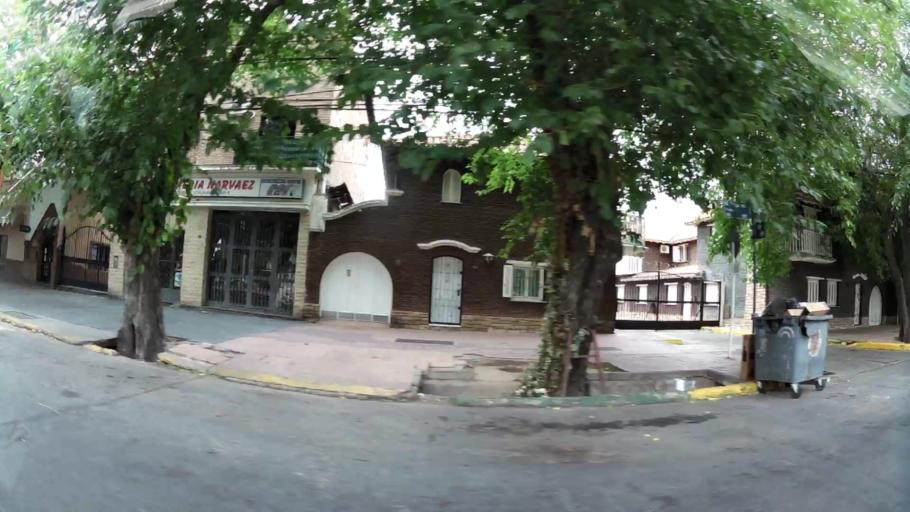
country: AR
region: Mendoza
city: Mendoza
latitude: -32.8942
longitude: -68.8511
